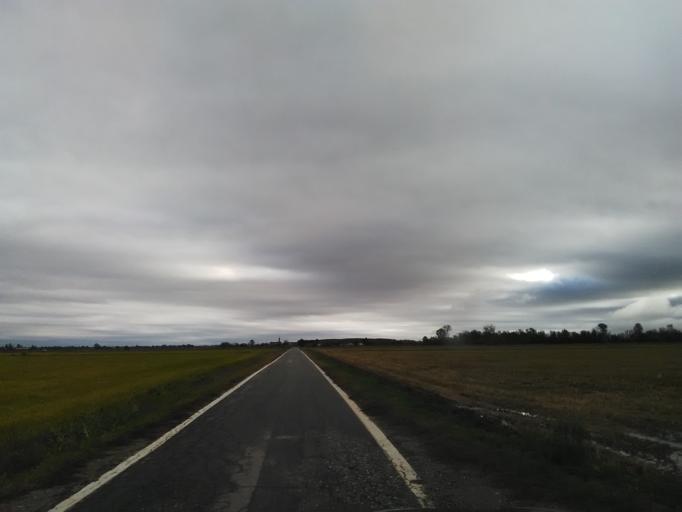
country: IT
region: Piedmont
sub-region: Provincia di Vercelli
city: Casanova Elvo
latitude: 45.4024
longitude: 8.2718
